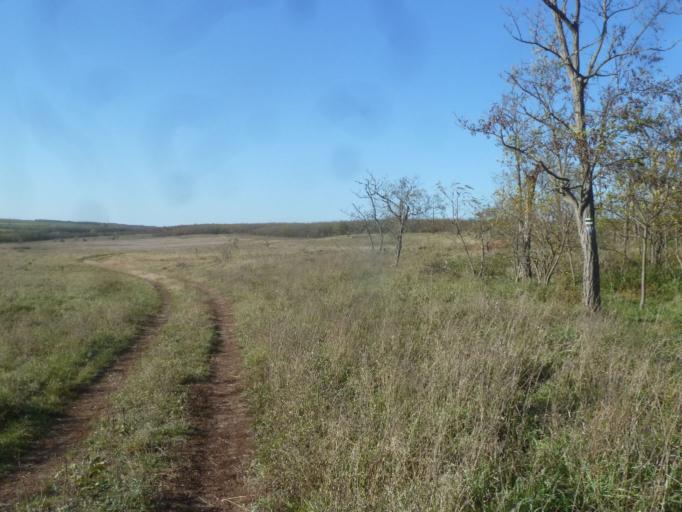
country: HU
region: Fejer
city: Pakozd
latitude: 47.2399
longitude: 18.5059
